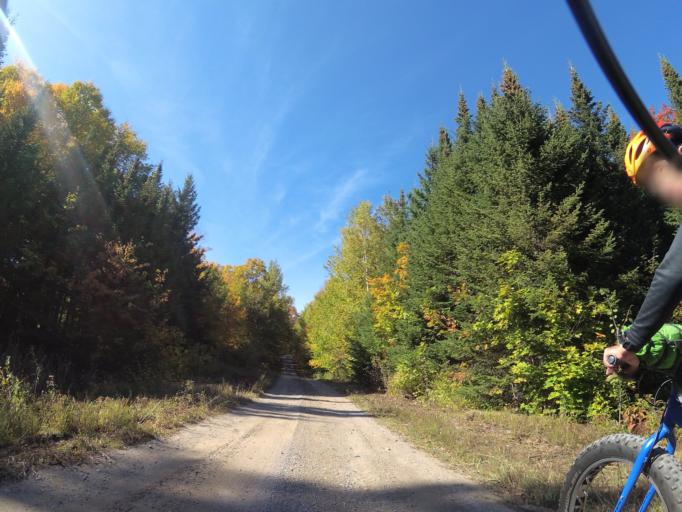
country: CA
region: Ontario
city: Renfrew
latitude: 45.3450
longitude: -77.0926
